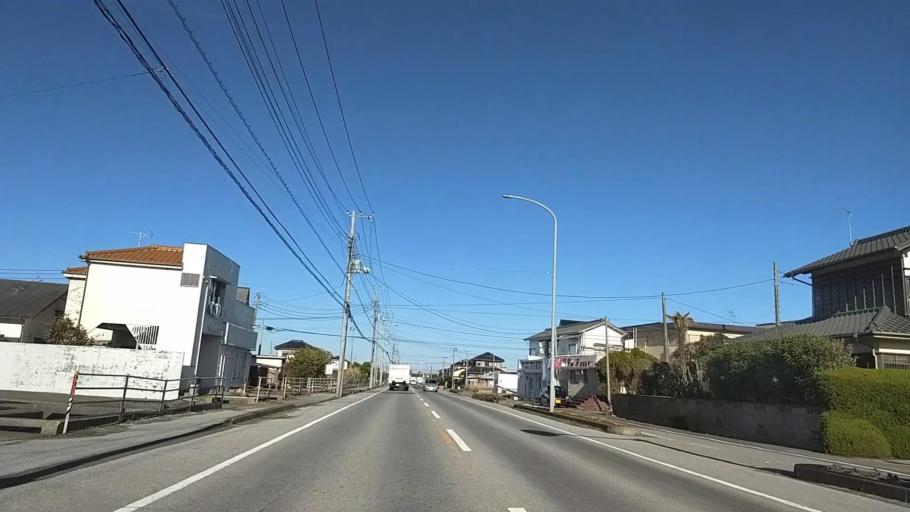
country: JP
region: Chiba
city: Togane
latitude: 35.5111
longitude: 140.4360
